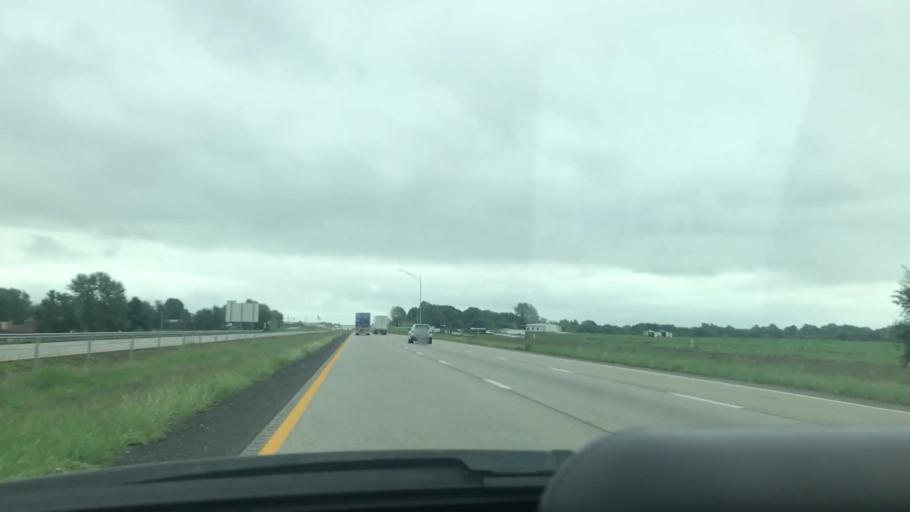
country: US
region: Missouri
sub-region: Greene County
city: Republic
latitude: 37.1970
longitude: -93.4398
